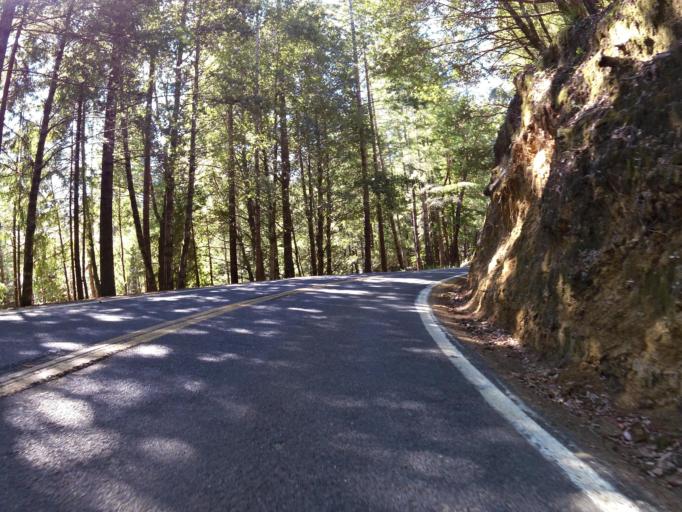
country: US
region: California
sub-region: Humboldt County
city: Redway
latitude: 39.8328
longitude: -123.7749
